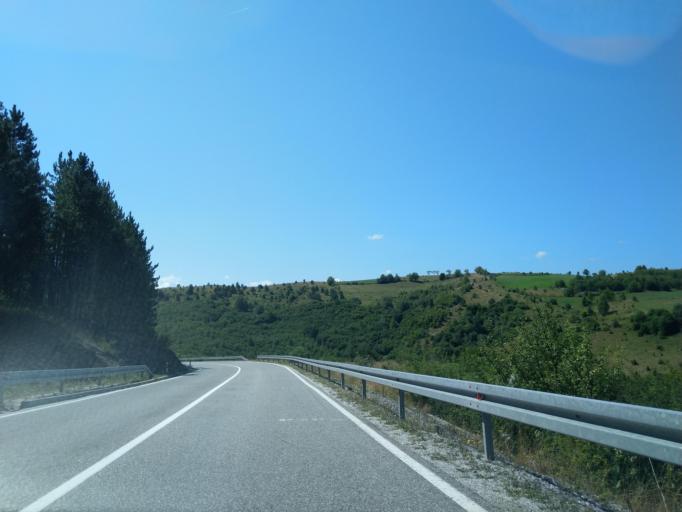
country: RS
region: Central Serbia
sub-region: Zlatiborski Okrug
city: Sjenica
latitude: 43.3035
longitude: 19.9298
